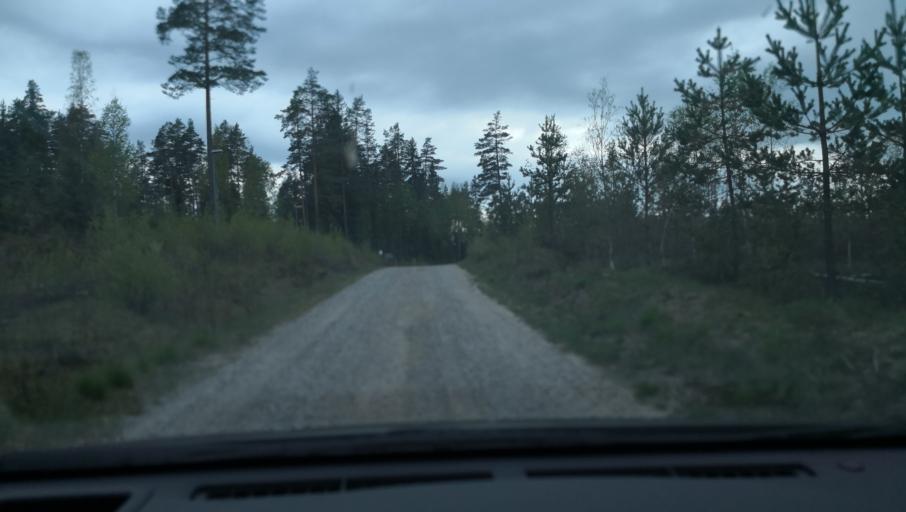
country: SE
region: Vaestmanland
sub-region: Skinnskattebergs Kommun
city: Skinnskatteberg
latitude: 59.8072
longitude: 15.5217
